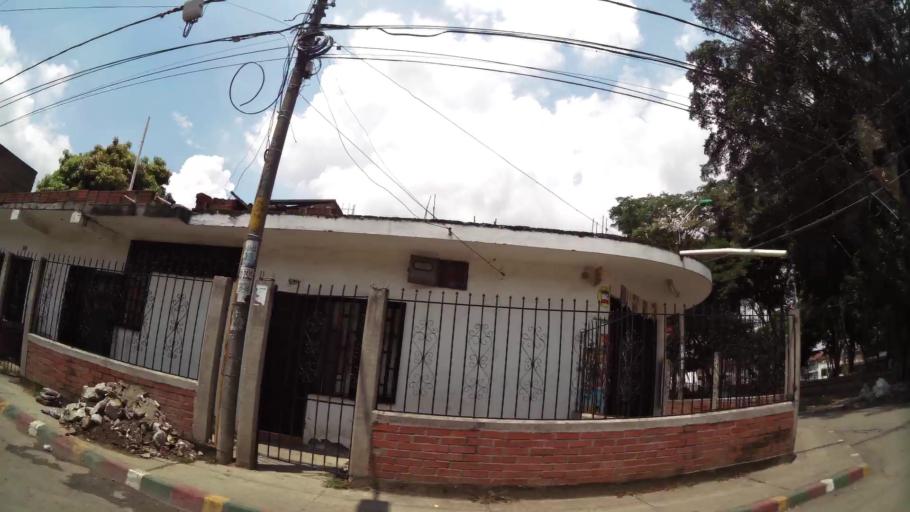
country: CO
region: Valle del Cauca
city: Cali
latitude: 3.4486
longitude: -76.4795
